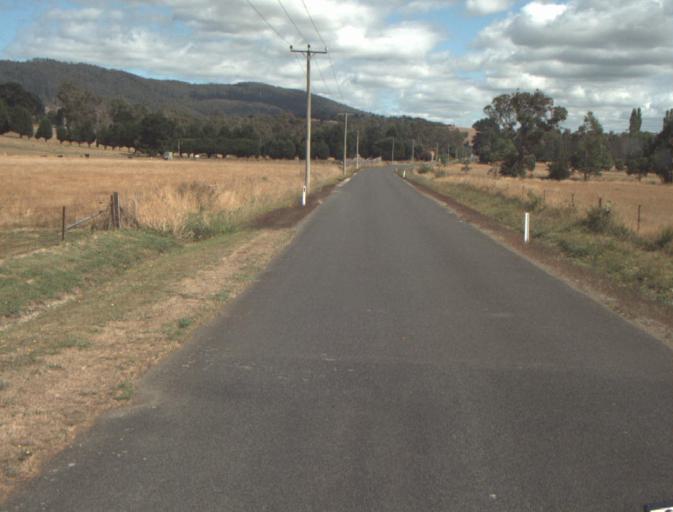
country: AU
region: Tasmania
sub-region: Launceston
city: Mayfield
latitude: -41.2605
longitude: 147.1570
